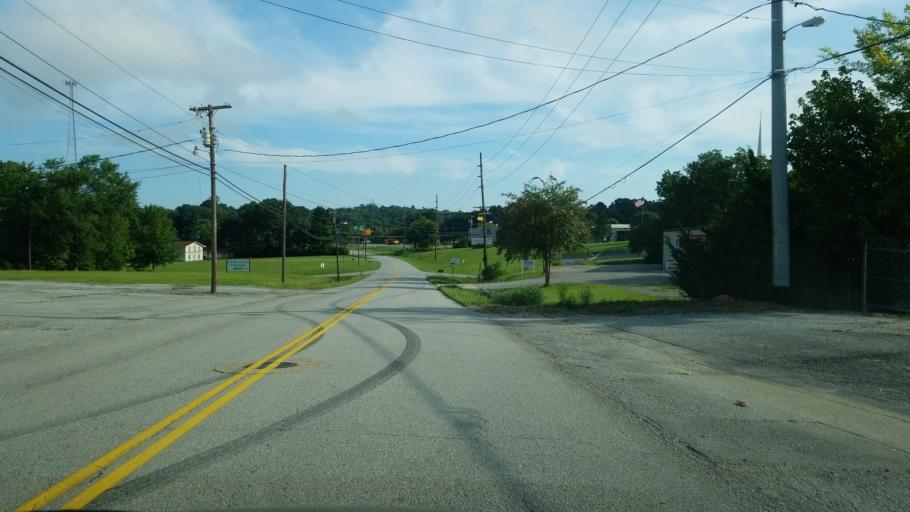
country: US
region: Tennessee
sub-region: Hamilton County
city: East Chattanooga
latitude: 35.0826
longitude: -85.2139
